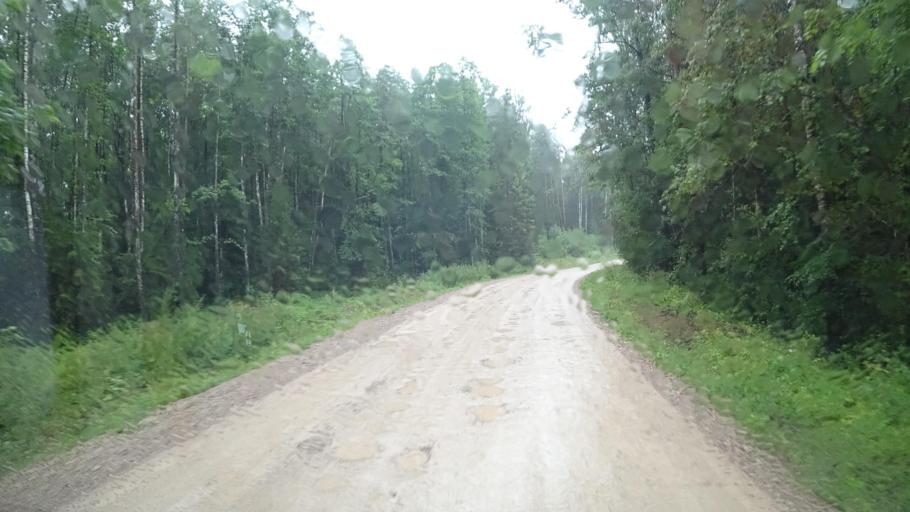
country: LV
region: Lecava
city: Iecava
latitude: 56.6598
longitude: 24.1741
